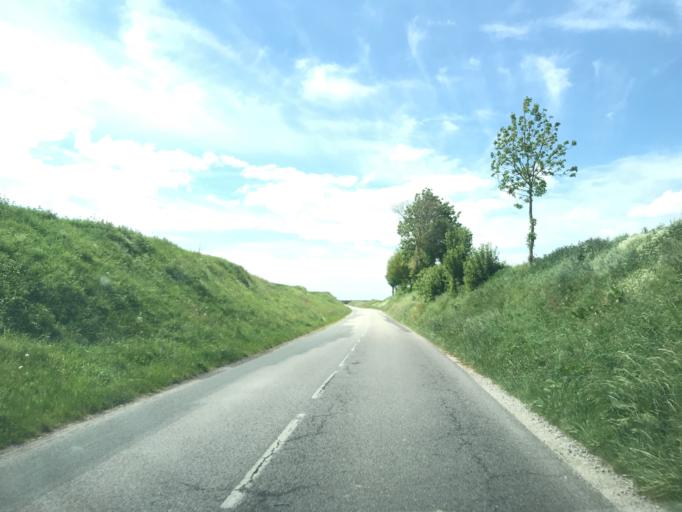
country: FR
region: Haute-Normandie
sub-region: Departement de l'Eure
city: Le Neubourg
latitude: 49.1482
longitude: 0.8902
